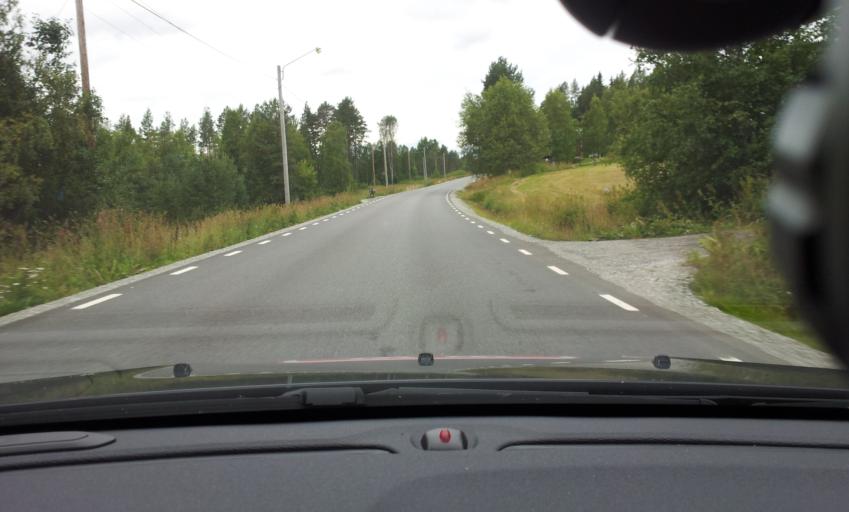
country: SE
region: Jaemtland
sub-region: Braecke Kommun
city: Braecke
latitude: 63.0772
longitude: 15.3894
